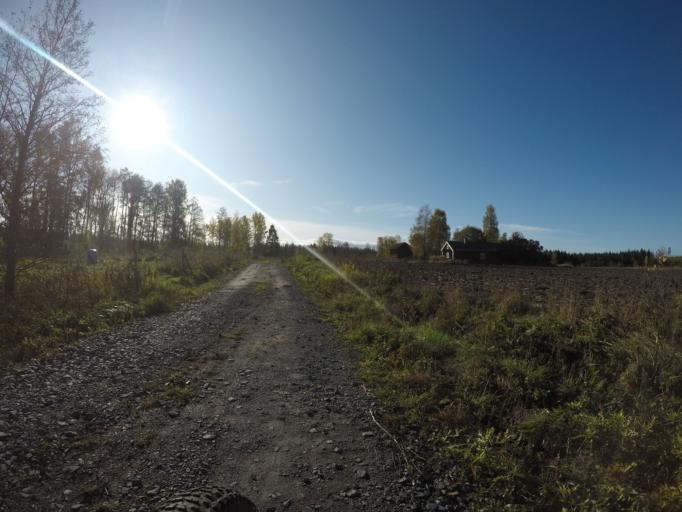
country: SE
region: Vaestmanland
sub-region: Kungsors Kommun
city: Kungsoer
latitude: 59.3252
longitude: 16.0956
